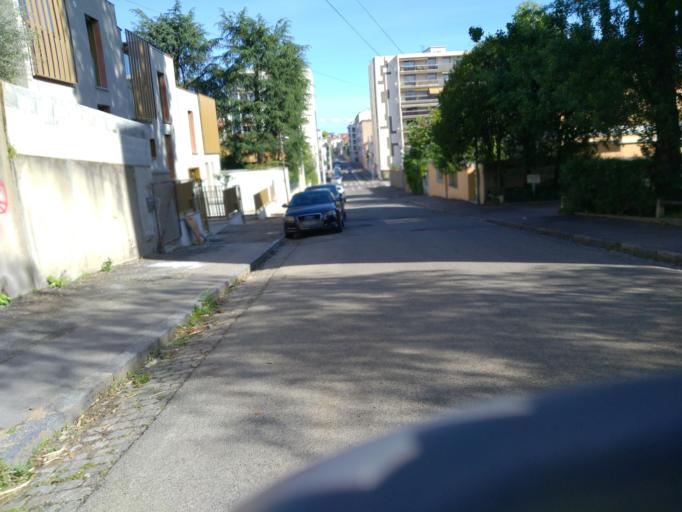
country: FR
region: Rhone-Alpes
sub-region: Departement du Rhone
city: Villeurbanne
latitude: 45.7491
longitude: 4.8901
